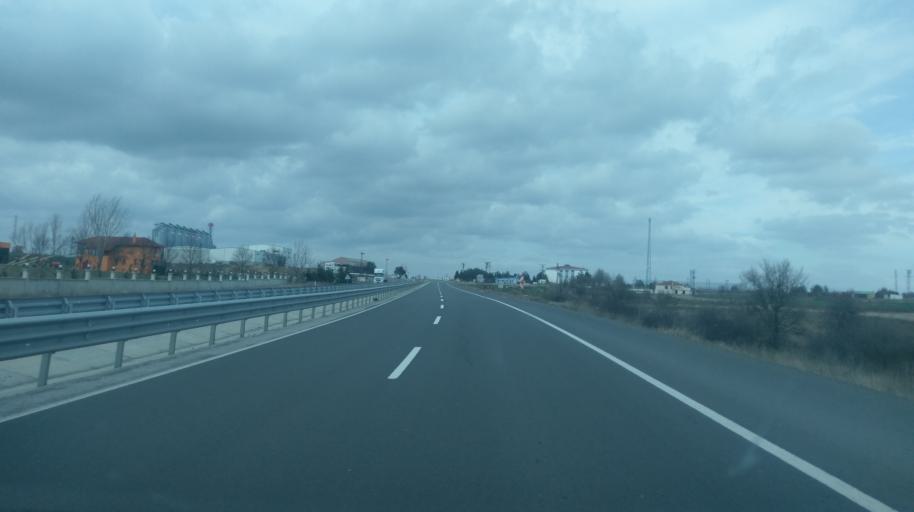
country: TR
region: Edirne
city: Hamidiye
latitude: 41.2047
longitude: 26.6782
